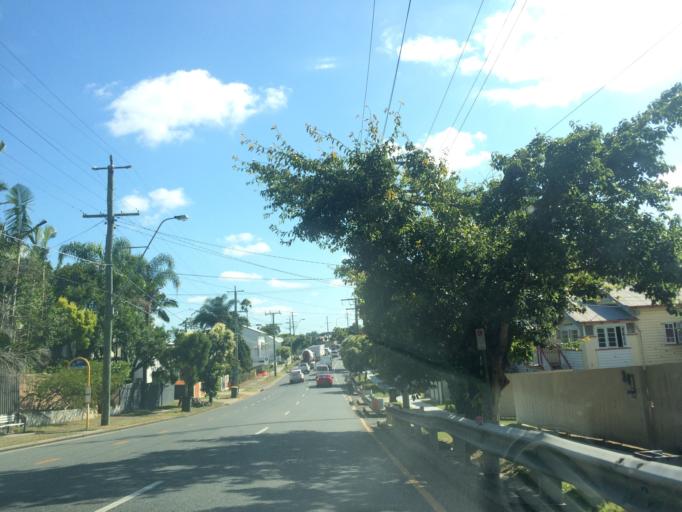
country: AU
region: Queensland
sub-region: Brisbane
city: Morningside
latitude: -27.4712
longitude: 153.0622
